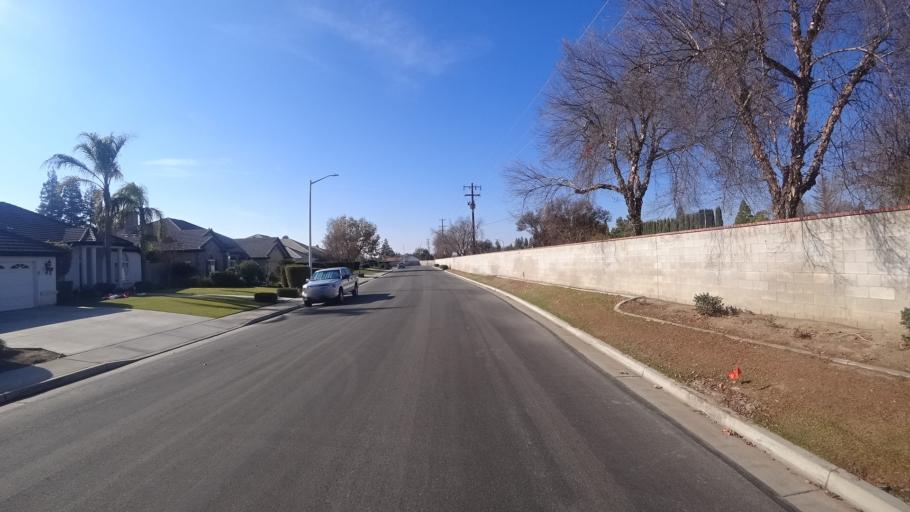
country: US
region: California
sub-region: Kern County
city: Greenacres
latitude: 35.3250
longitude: -119.1169
